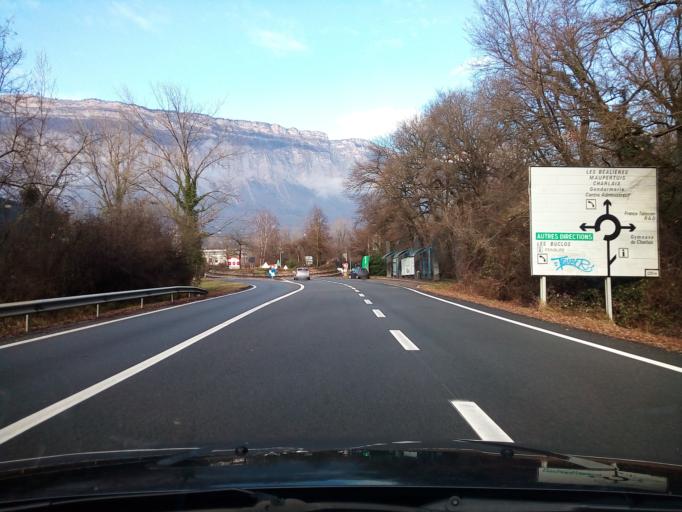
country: FR
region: Rhone-Alpes
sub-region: Departement de l'Isere
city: Meylan
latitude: 45.2079
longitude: 5.7920
